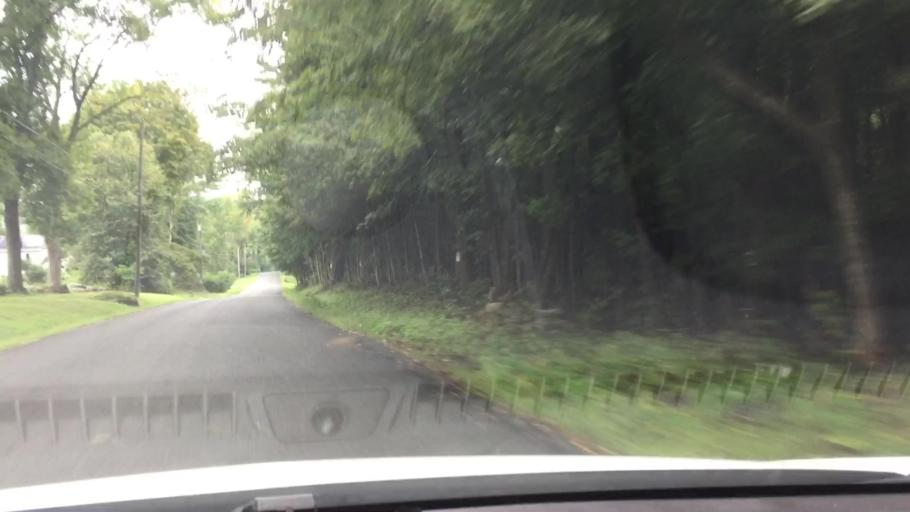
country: US
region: Massachusetts
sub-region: Berkshire County
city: Richmond
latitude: 42.3624
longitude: -73.3681
